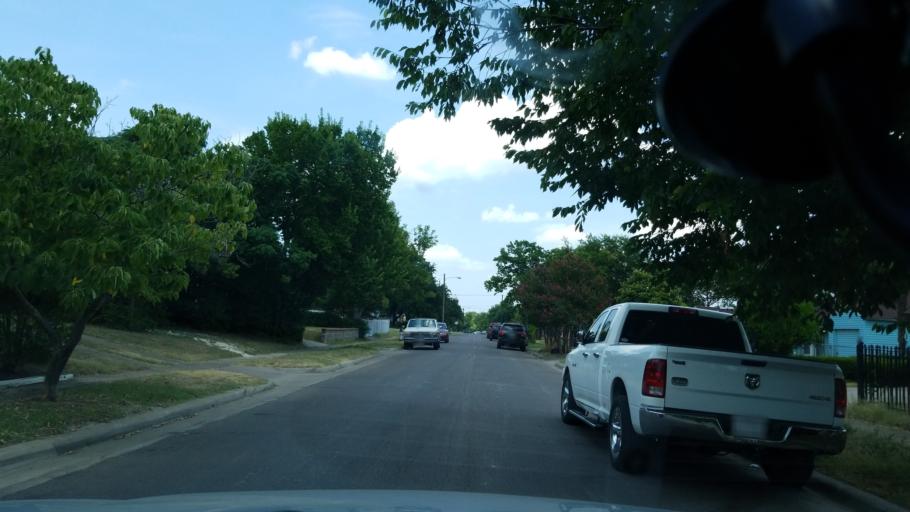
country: US
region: Texas
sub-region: Dallas County
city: Cockrell Hill
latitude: 32.7245
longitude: -96.8710
